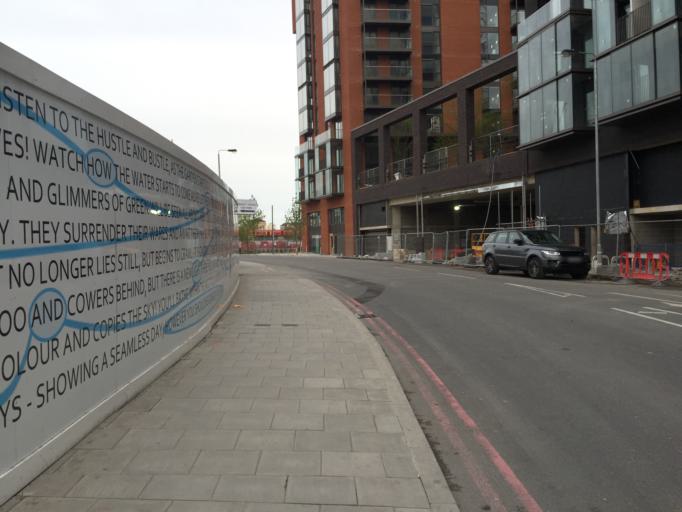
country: GB
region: England
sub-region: Greater London
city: Battersea
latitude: 51.4825
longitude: -0.1343
